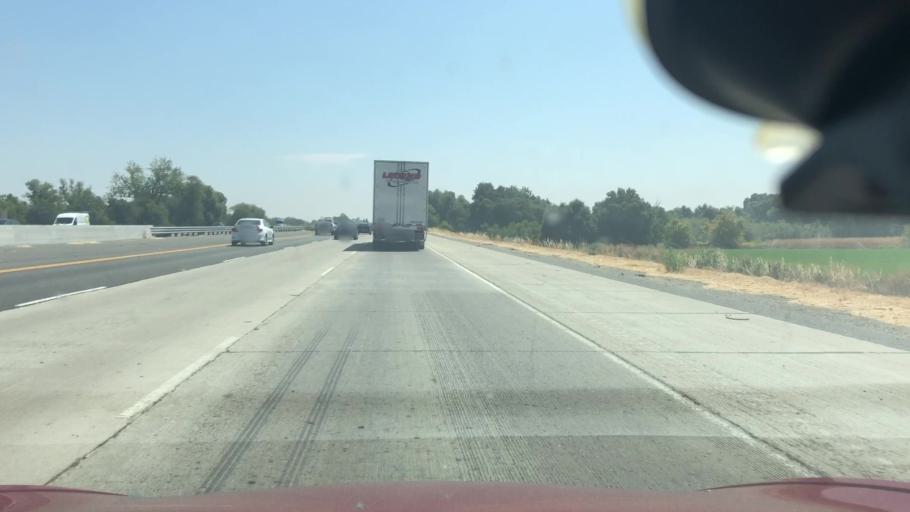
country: US
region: California
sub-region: Sacramento County
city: Parkway
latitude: 38.4420
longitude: -121.4909
